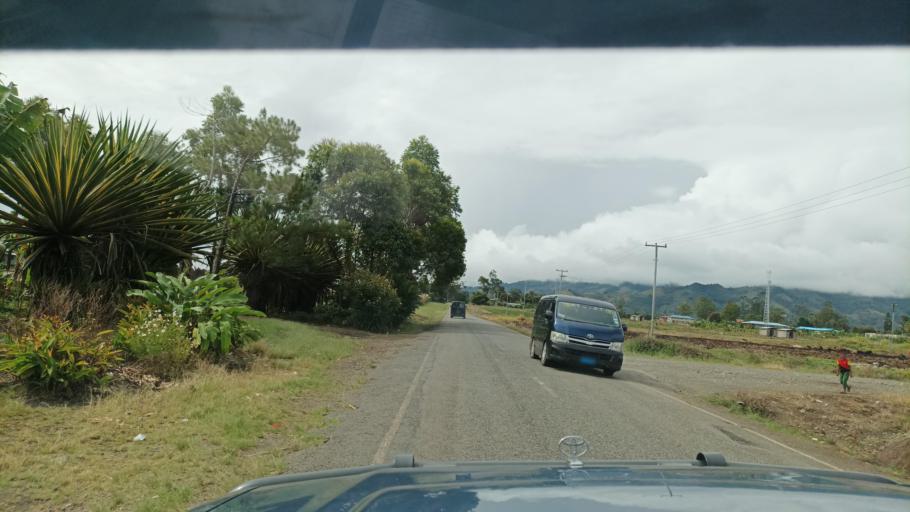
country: PG
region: Jiwaka
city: Minj
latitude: -5.9017
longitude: 144.6878
